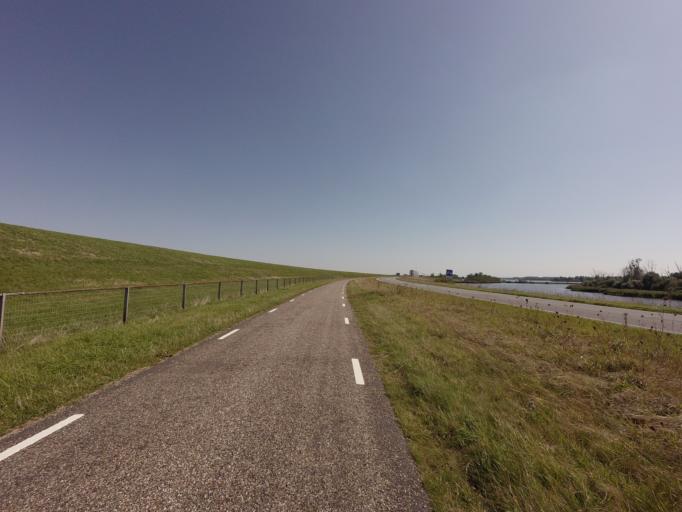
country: NL
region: Friesland
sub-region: Gemeente Dongeradeel
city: Anjum
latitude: 53.4140
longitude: 6.1823
